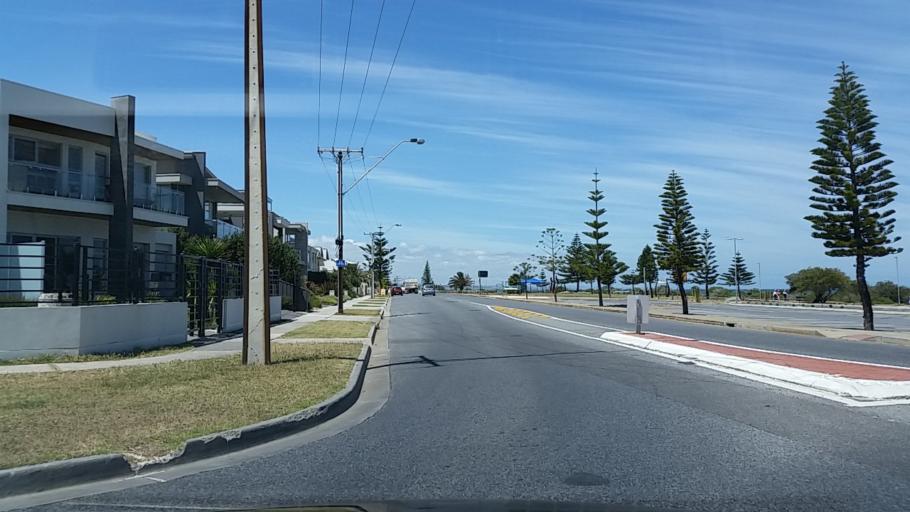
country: AU
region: South Australia
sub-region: Charles Sturt
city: Henley Beach
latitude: -34.9381
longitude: 138.5001
